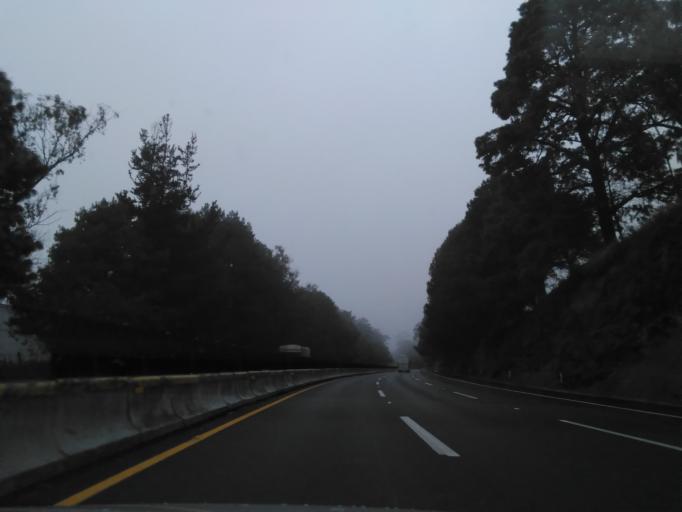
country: MX
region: Mexico City
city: Xochimilco
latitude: 19.1834
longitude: -99.1558
